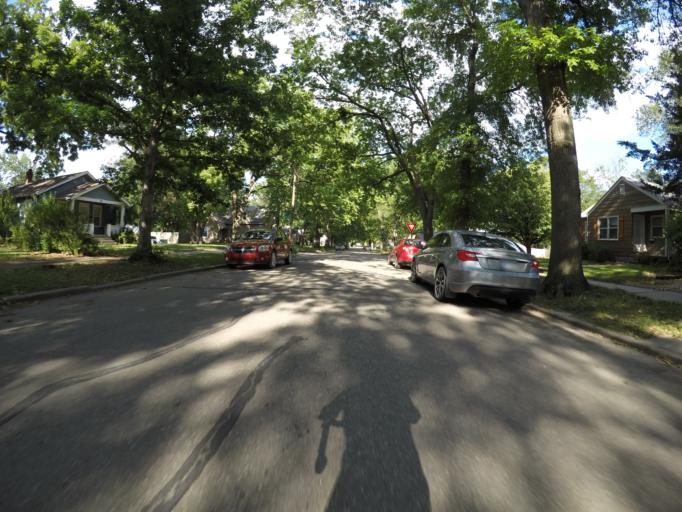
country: US
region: Kansas
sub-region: Riley County
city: Manhattan
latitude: 39.1899
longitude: -96.5687
